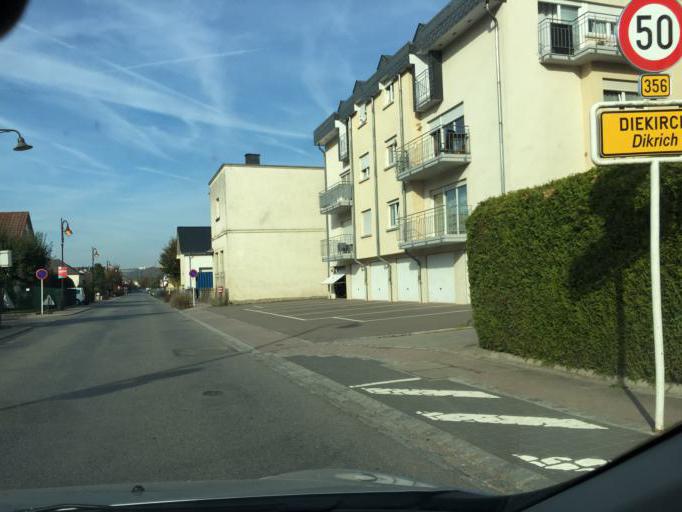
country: LU
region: Diekirch
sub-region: Canton de Diekirch
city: Diekirch
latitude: 49.8643
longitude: 6.1760
